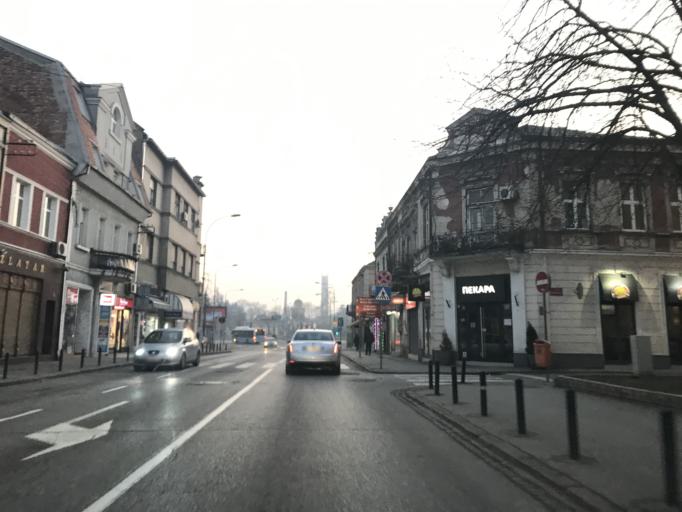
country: RS
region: Central Serbia
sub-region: Sumadijski Okrug
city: Kragujevac
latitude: 44.0103
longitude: 20.9151
